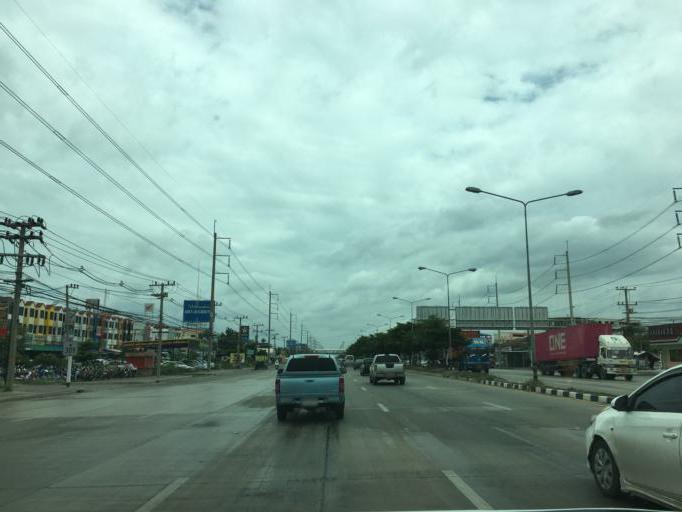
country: TH
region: Phra Nakhon Si Ayutthaya
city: Uthai
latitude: 14.3114
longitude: 100.6423
